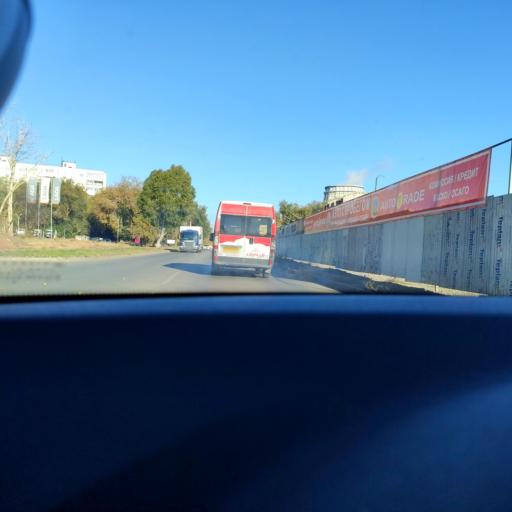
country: RU
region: Samara
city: Petra-Dubrava
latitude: 53.2449
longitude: 50.2703
